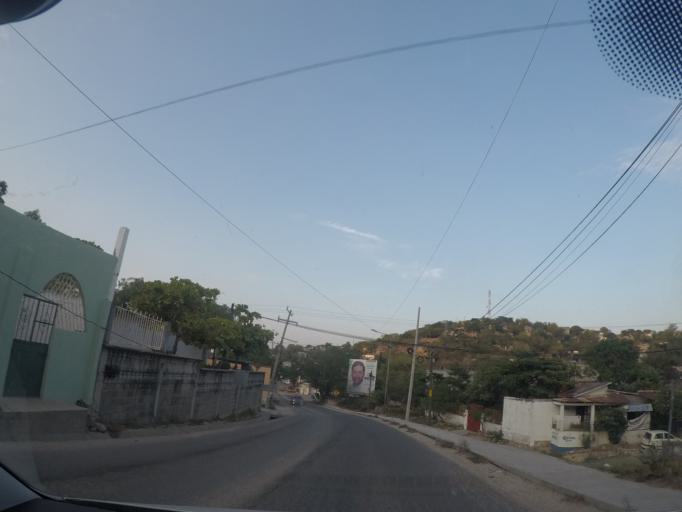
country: MX
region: Oaxaca
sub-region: Salina Cruz
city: Salina Cruz
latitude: 16.1949
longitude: -95.2037
